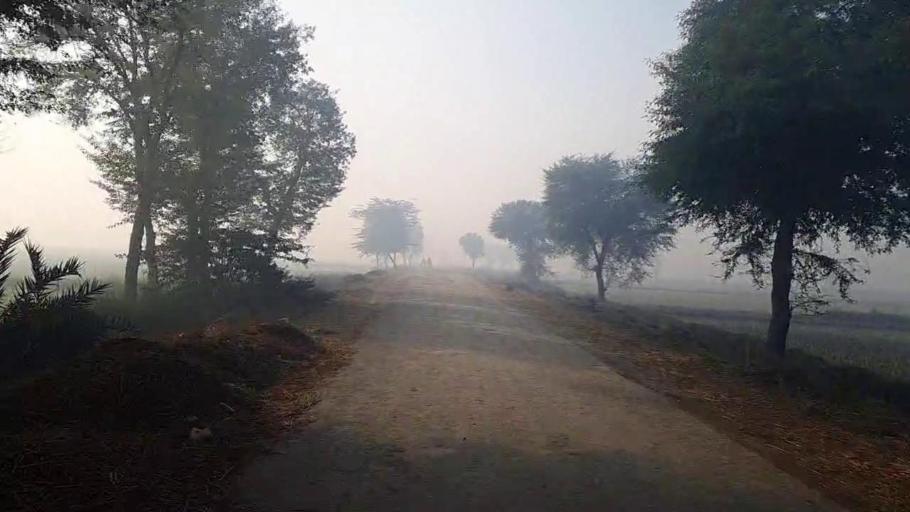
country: PK
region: Sindh
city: Mehar
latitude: 27.1588
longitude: 67.8240
